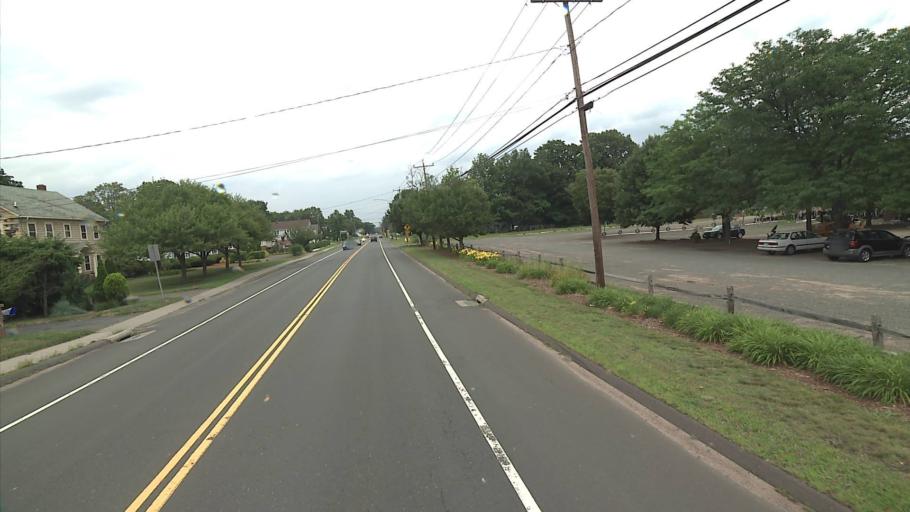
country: US
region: Connecticut
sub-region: Middlesex County
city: Cromwell
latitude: 41.6255
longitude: -72.6527
